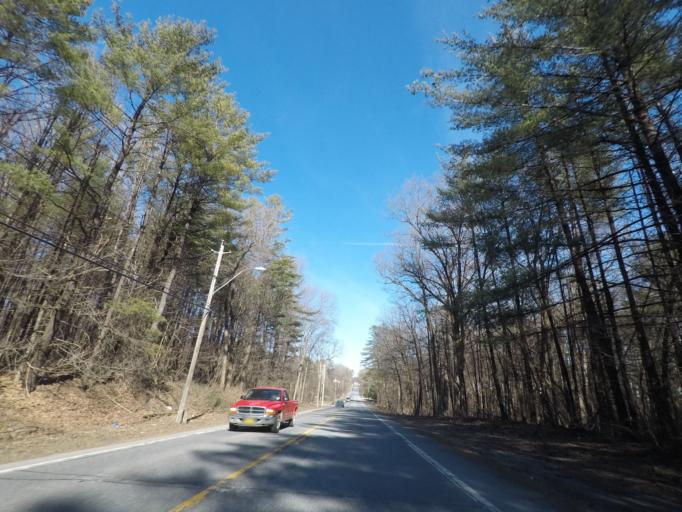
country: US
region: New York
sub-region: Saratoga County
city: Saratoga Springs
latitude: 43.0765
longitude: -73.8308
